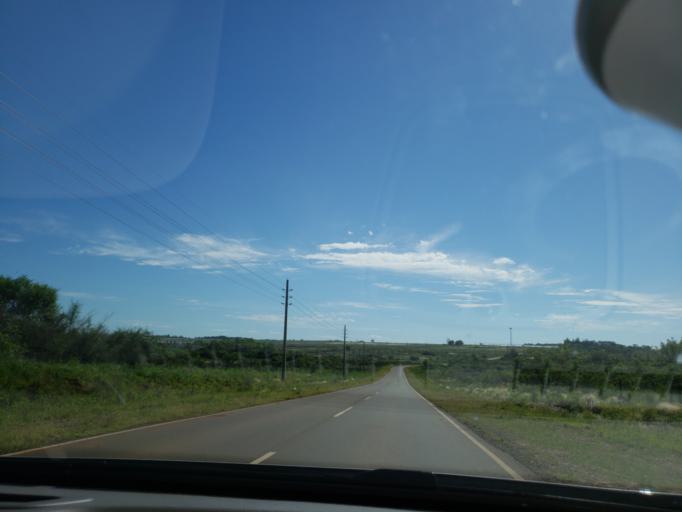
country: AR
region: Misiones
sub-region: Departamento de Capital
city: Posadas
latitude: -27.3891
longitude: -55.9815
